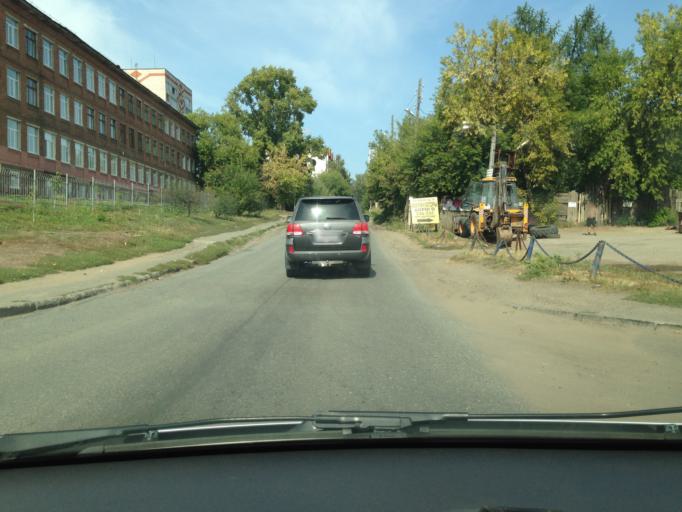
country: RU
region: Udmurtiya
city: Izhevsk
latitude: 56.8615
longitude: 53.1882
